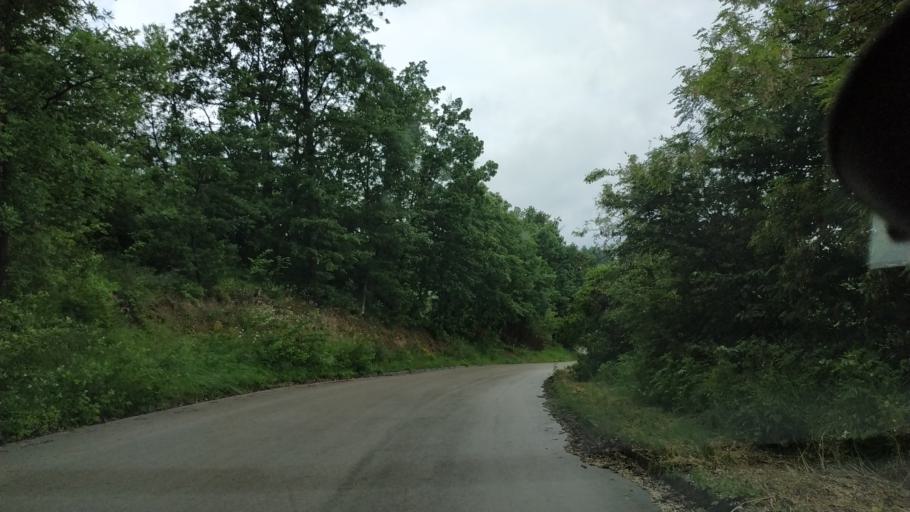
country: RS
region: Central Serbia
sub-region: Toplicki Okrug
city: Prokuplje
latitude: 43.4140
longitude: 21.5543
